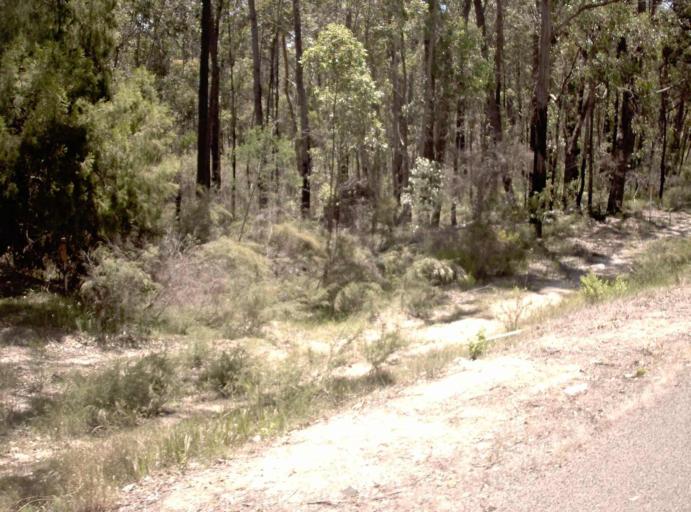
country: AU
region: Victoria
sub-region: East Gippsland
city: Lakes Entrance
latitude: -37.7702
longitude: 148.0583
